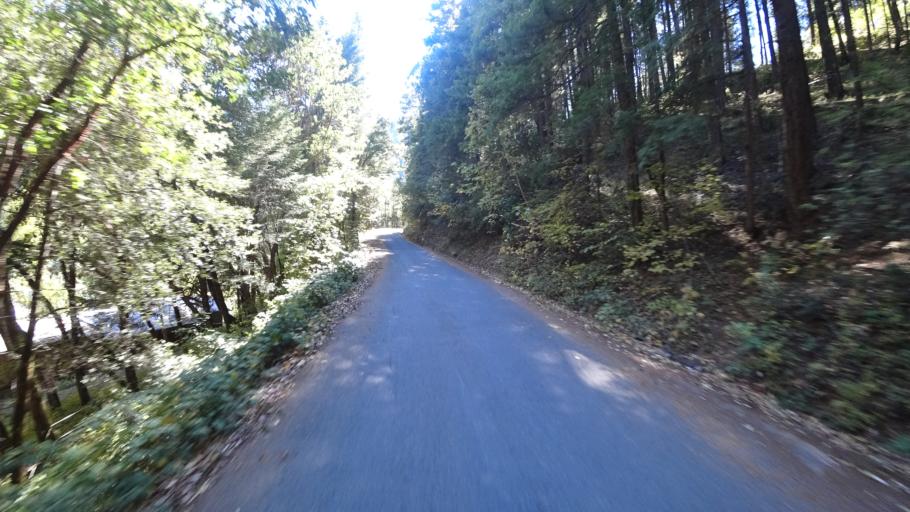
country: US
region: California
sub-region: Siskiyou County
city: Happy Camp
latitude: 41.3166
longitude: -123.1793
